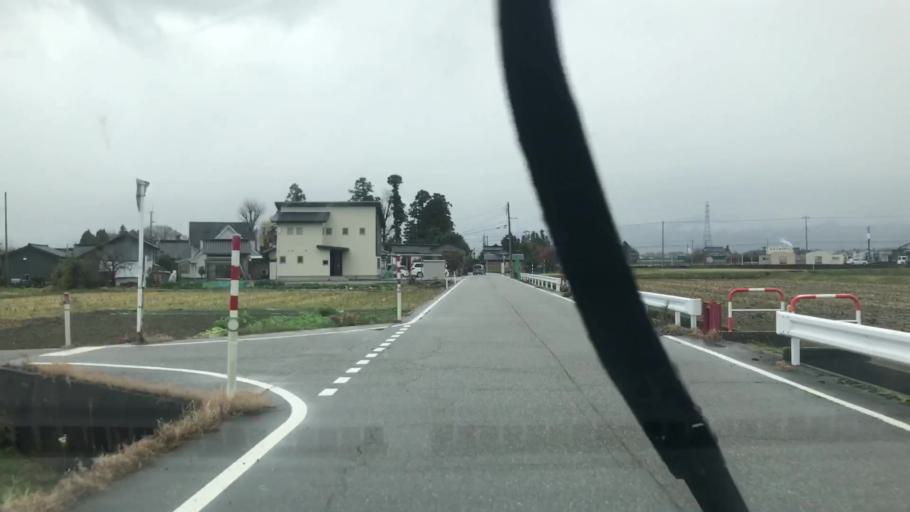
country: JP
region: Toyama
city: Toyama-shi
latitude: 36.6743
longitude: 137.2867
